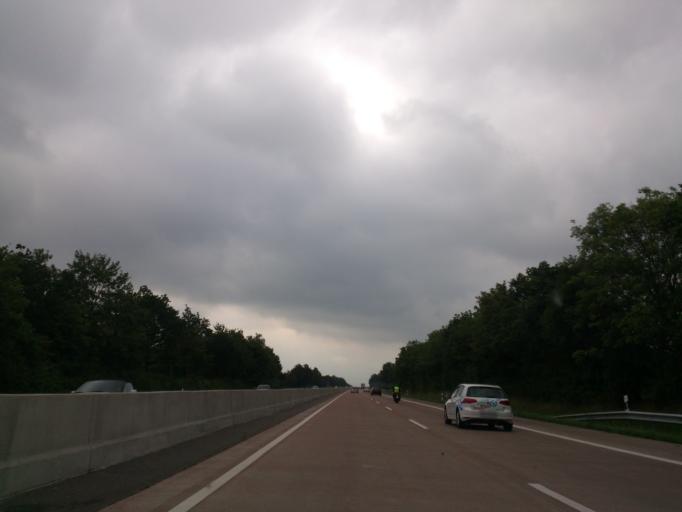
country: DE
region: Schleswig-Holstein
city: Horst
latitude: 53.8290
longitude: 9.6325
